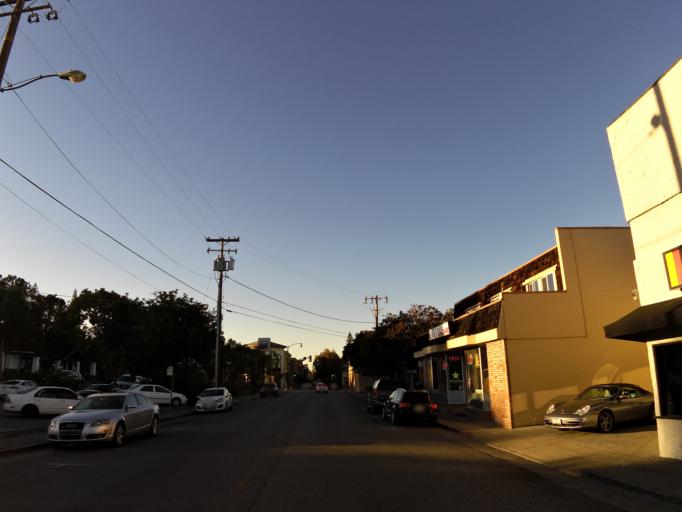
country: US
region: California
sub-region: Santa Clara County
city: Los Altos
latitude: 37.3769
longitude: -122.1170
